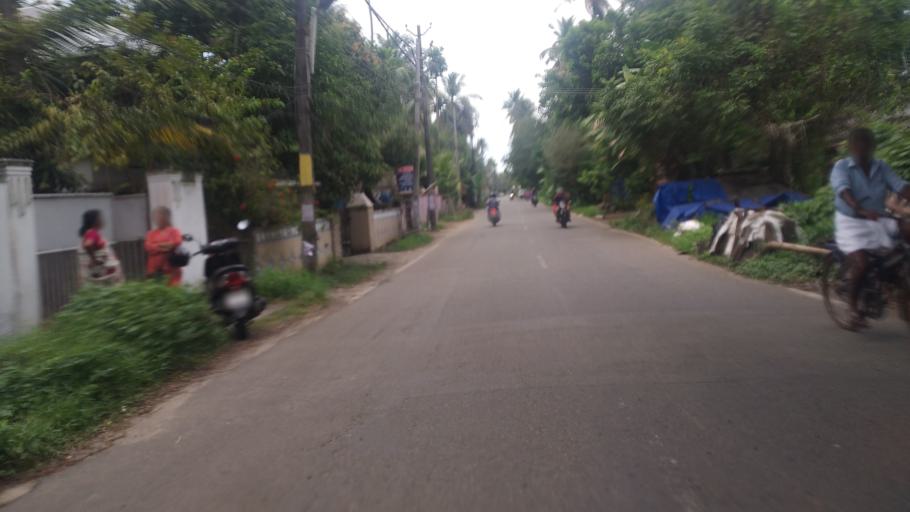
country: IN
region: Kerala
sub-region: Ernakulam
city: Cochin
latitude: 9.8836
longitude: 76.2619
